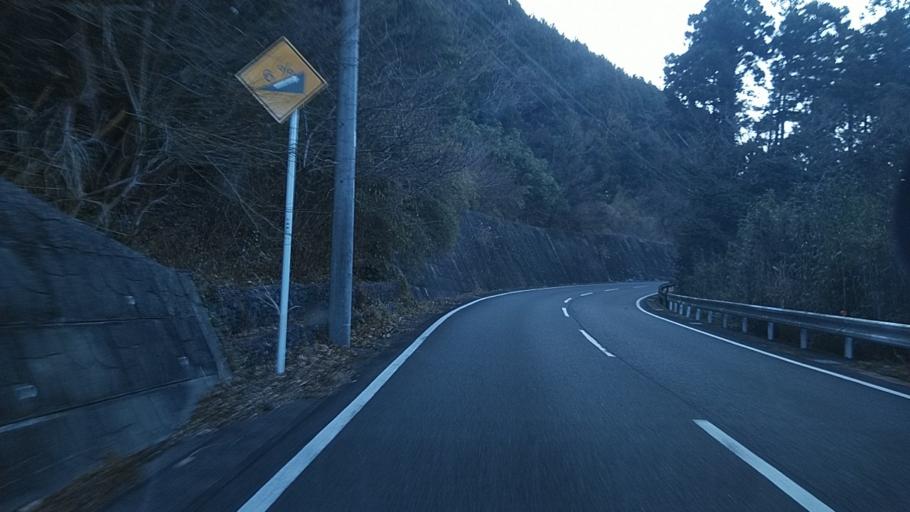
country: JP
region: Chiba
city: Kimitsu
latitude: 35.2601
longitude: 139.9337
